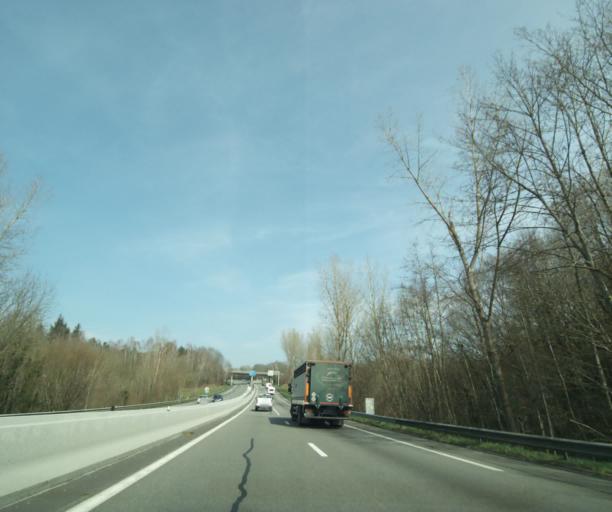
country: FR
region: Limousin
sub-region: Departement de la Haute-Vienne
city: Condat-sur-Vienne
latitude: 45.8046
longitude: 1.2973
